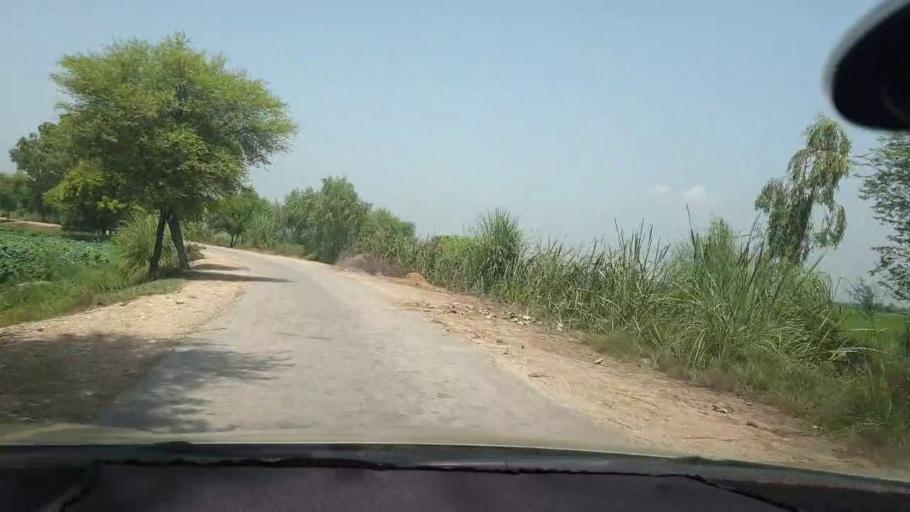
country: PK
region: Sindh
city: Kambar
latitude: 27.6617
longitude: 67.9478
